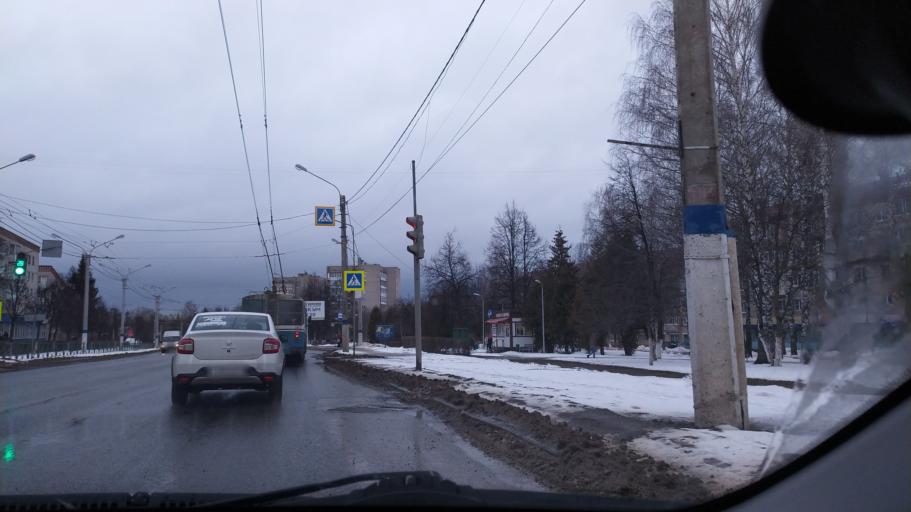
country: RU
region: Chuvashia
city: Novocheboksarsk
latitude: 56.1177
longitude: 47.4924
